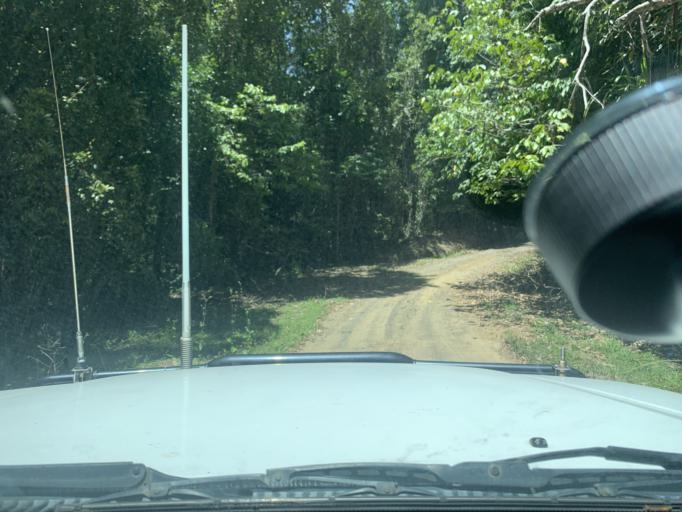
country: AU
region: Queensland
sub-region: Cairns
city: Redlynch
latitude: -16.9605
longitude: 145.6458
